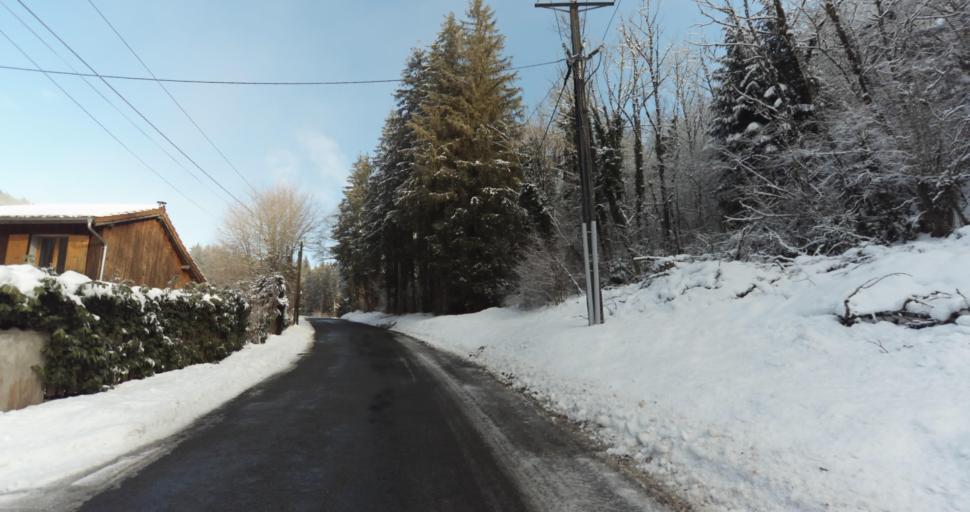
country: FR
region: Rhone-Alpes
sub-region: Departement de l'Ain
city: Nantua
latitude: 46.1573
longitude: 5.6268
